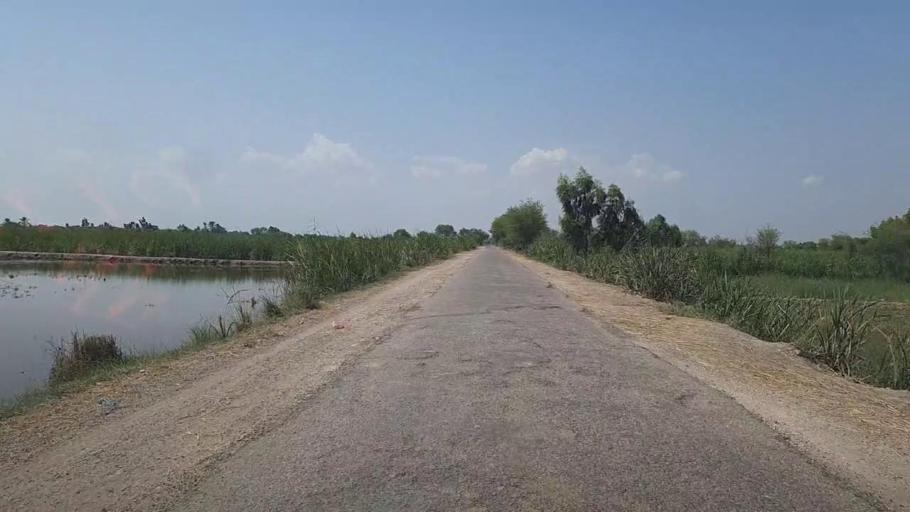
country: PK
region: Sindh
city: Khairpur
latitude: 28.0725
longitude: 69.6406
